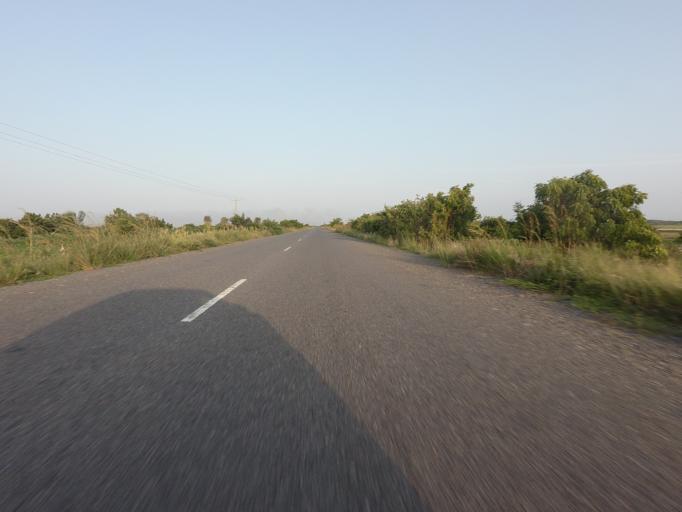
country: GH
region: Volta
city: Anloga
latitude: 5.8532
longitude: 0.7705
